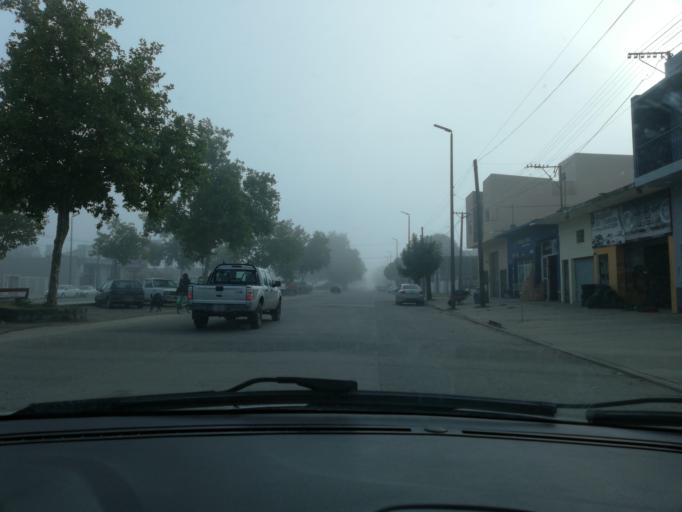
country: AR
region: Buenos Aires
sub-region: Partido de Balcarce
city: Balcarce
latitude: -37.8549
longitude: -58.2657
